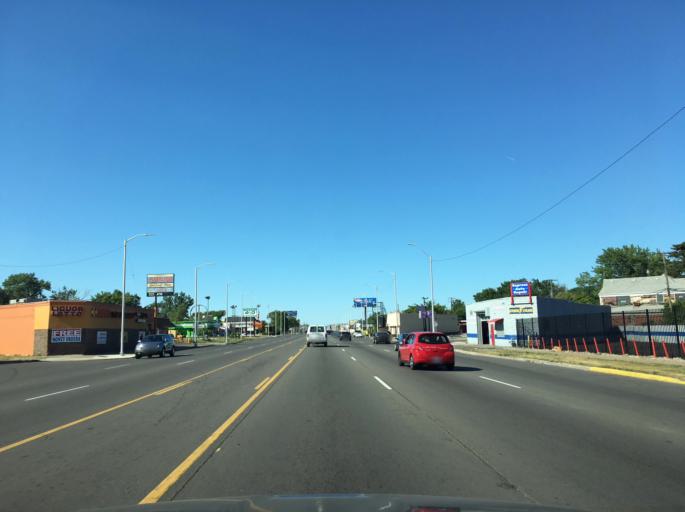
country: US
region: Michigan
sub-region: Wayne County
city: Hamtramck
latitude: 42.4109
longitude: -82.9935
